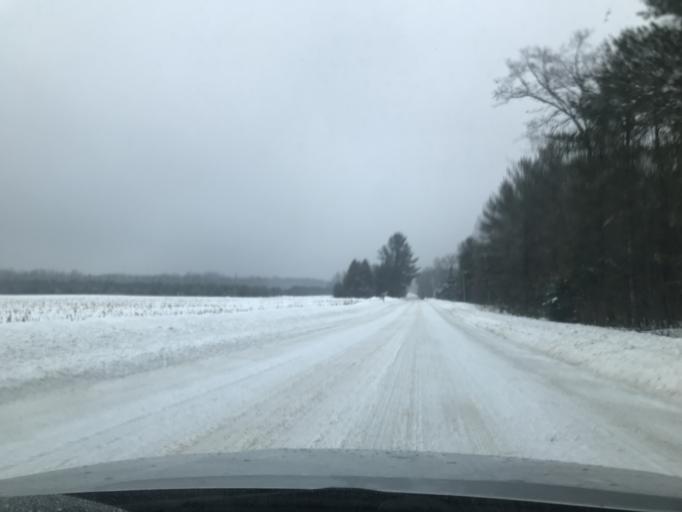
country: US
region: Wisconsin
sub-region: Marinette County
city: Peshtigo
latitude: 45.3812
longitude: -87.9392
